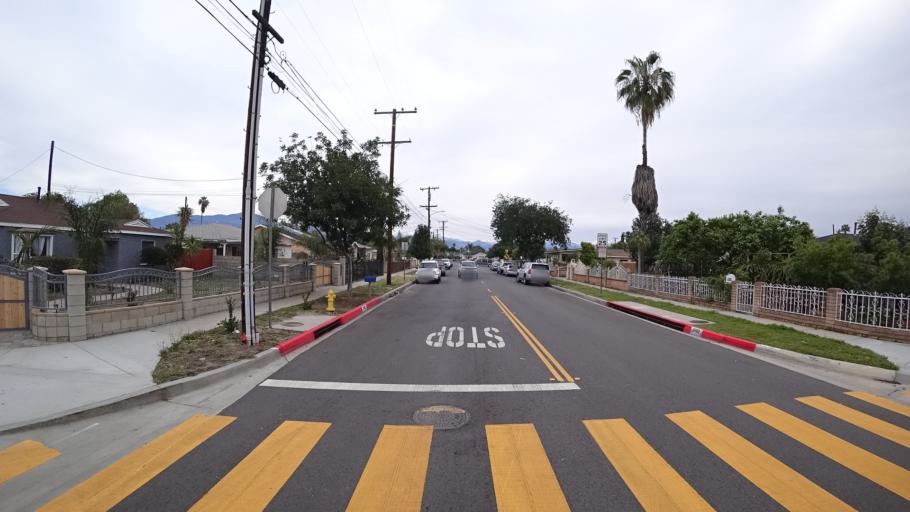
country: US
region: California
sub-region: Los Angeles County
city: West Puente Valley
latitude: 34.0712
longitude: -117.9905
